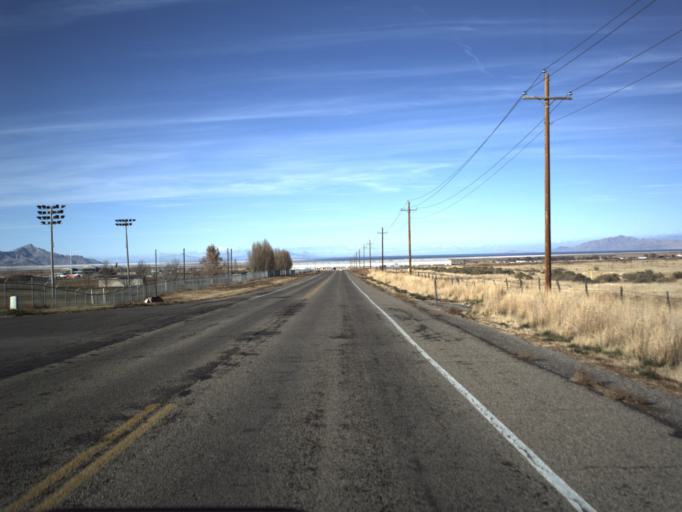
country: US
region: Utah
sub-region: Tooele County
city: Erda
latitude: 40.5699
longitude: -112.3672
